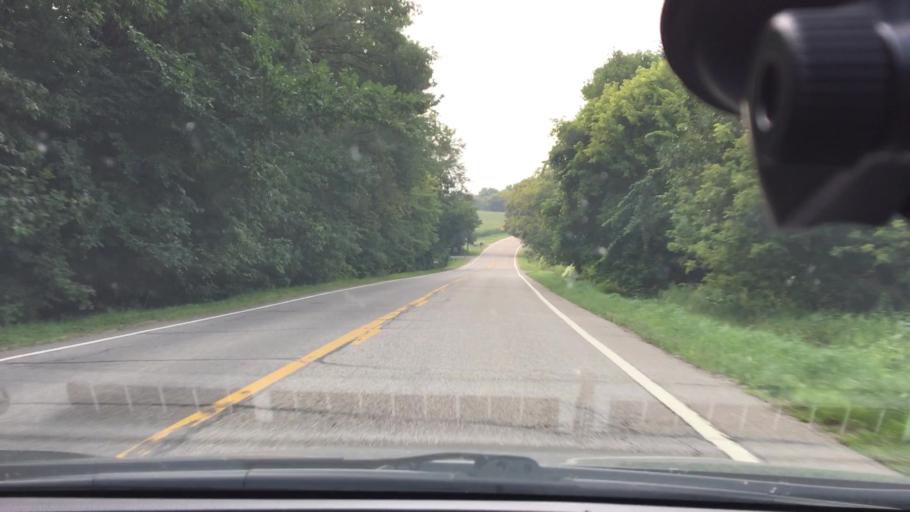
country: US
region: Minnesota
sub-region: Hennepin County
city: Dayton
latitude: 45.2241
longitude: -93.4857
